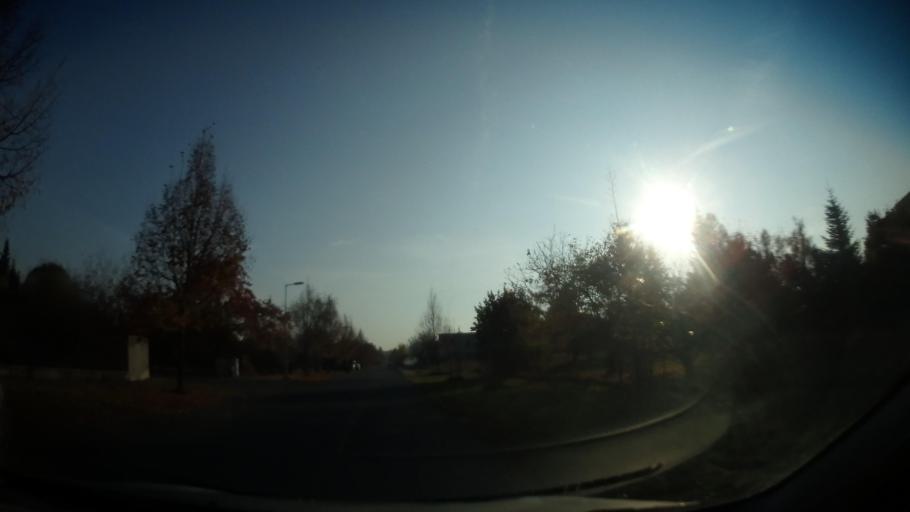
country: CZ
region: Central Bohemia
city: Sestajovice
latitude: 50.1015
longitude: 14.6806
